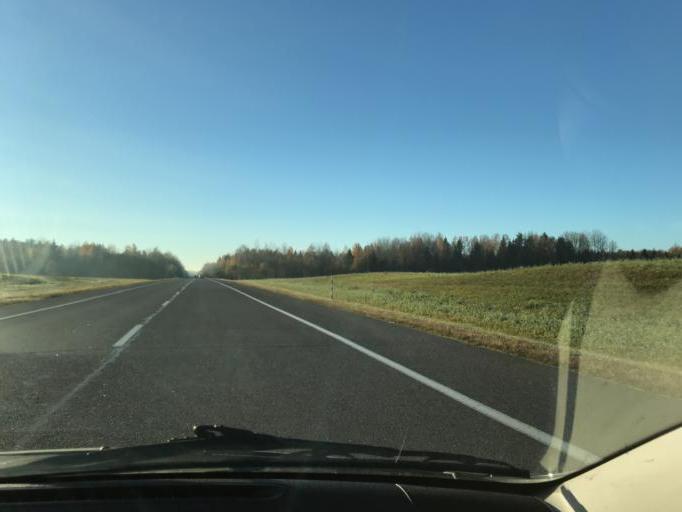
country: BY
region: Vitebsk
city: Vitebsk
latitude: 54.9897
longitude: 30.3420
